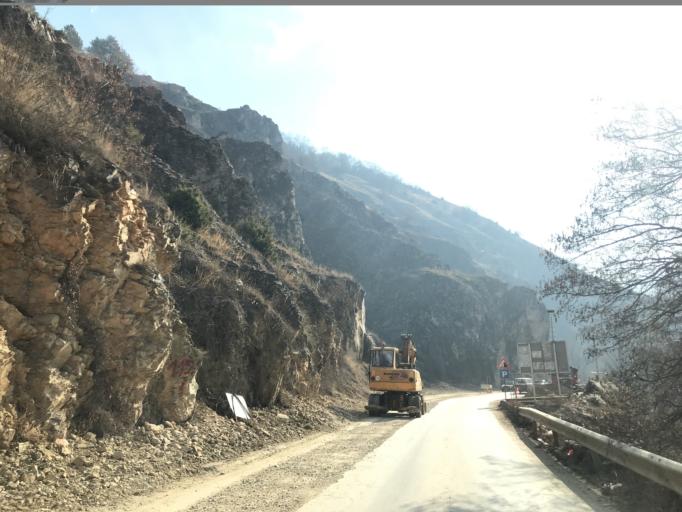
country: XK
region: Prizren
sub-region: Prizren
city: Prizren
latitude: 42.2099
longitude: 20.7495
